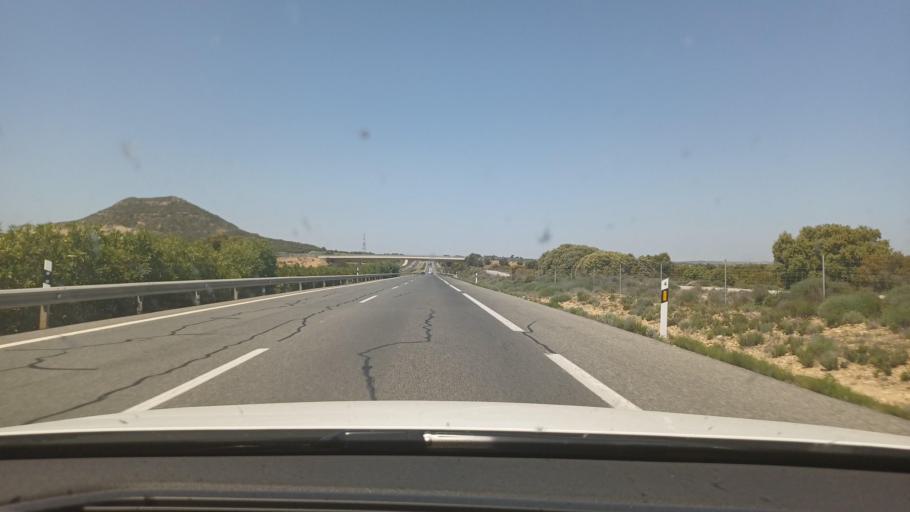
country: ES
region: Castille-La Mancha
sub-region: Provincia de Albacete
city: Corral-Rubio
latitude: 38.8986
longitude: -1.4516
